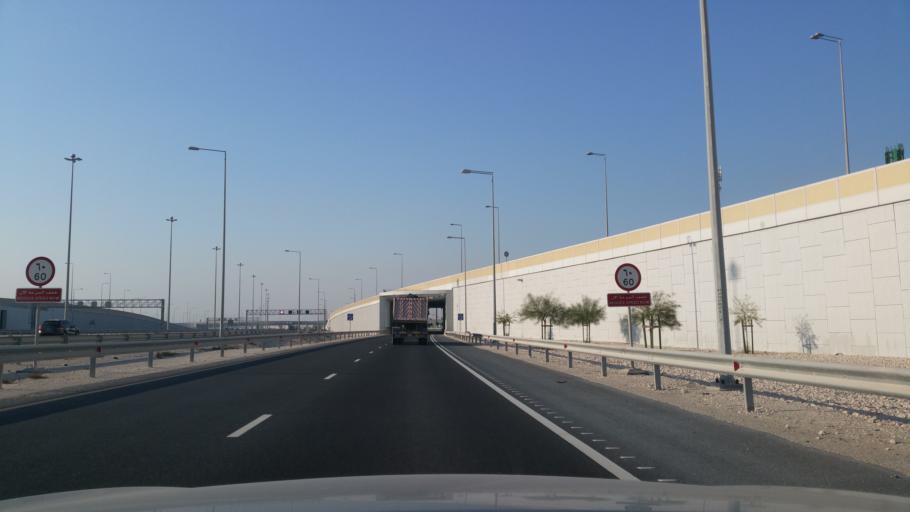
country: QA
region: Al Wakrah
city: Al Wakrah
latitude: 25.1550
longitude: 51.5735
